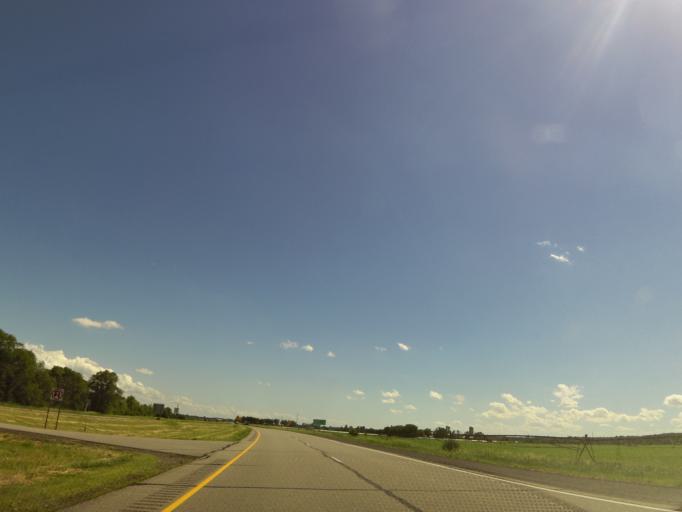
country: US
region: Minnesota
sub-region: Stearns County
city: Saint Augusta
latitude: 45.4890
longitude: -94.2465
